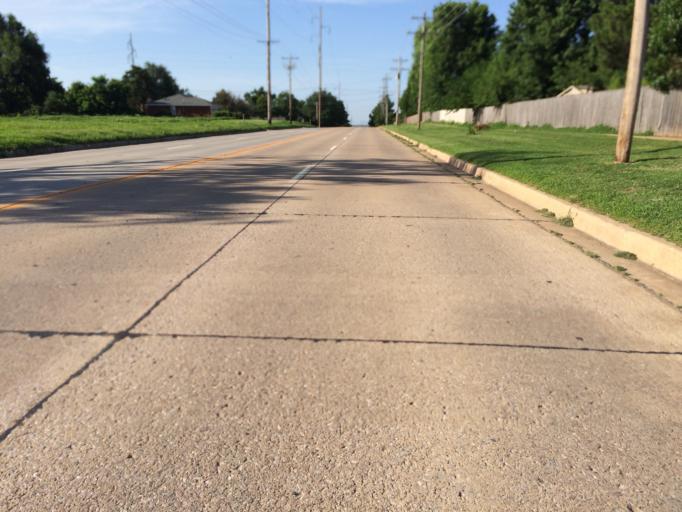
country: US
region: Oklahoma
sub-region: Cleveland County
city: Norman
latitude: 35.2126
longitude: -97.4943
